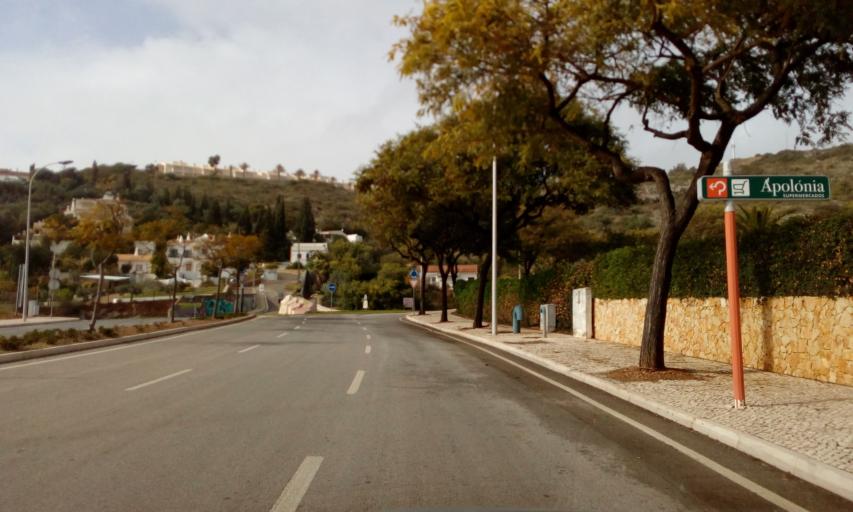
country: PT
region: Faro
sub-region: Albufeira
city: Albufeira
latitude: 37.0871
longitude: -8.2701
